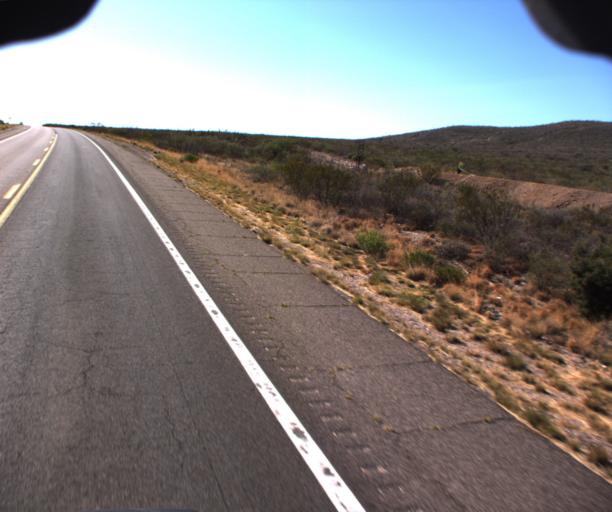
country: US
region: Arizona
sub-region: Cochise County
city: Tombstone
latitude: 31.6926
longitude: -110.0399
